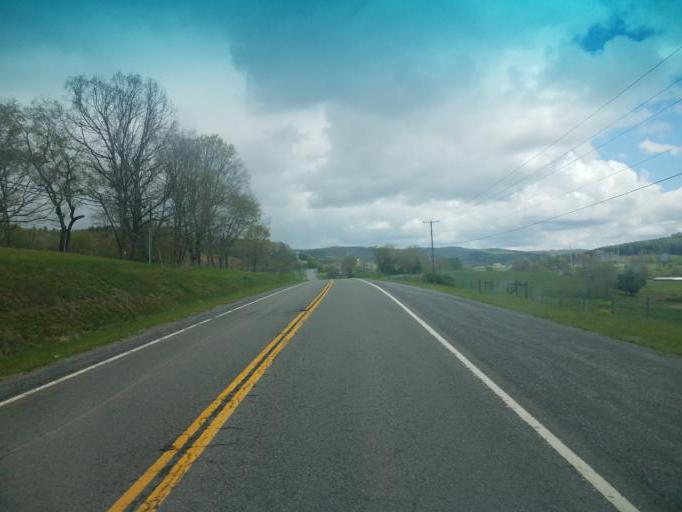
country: US
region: Virginia
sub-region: Bland County
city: Bland
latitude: 37.0932
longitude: -81.1370
